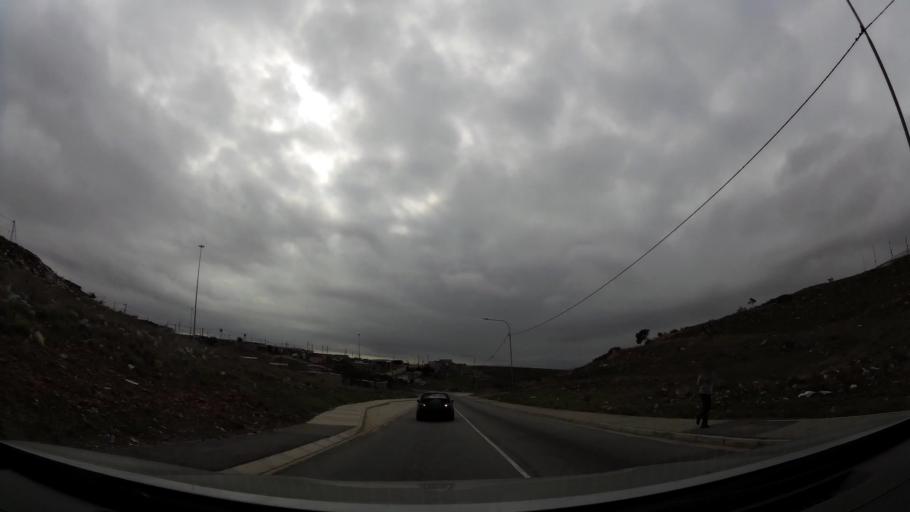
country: ZA
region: Eastern Cape
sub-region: Nelson Mandela Bay Metropolitan Municipality
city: Port Elizabeth
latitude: -33.9126
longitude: 25.5381
